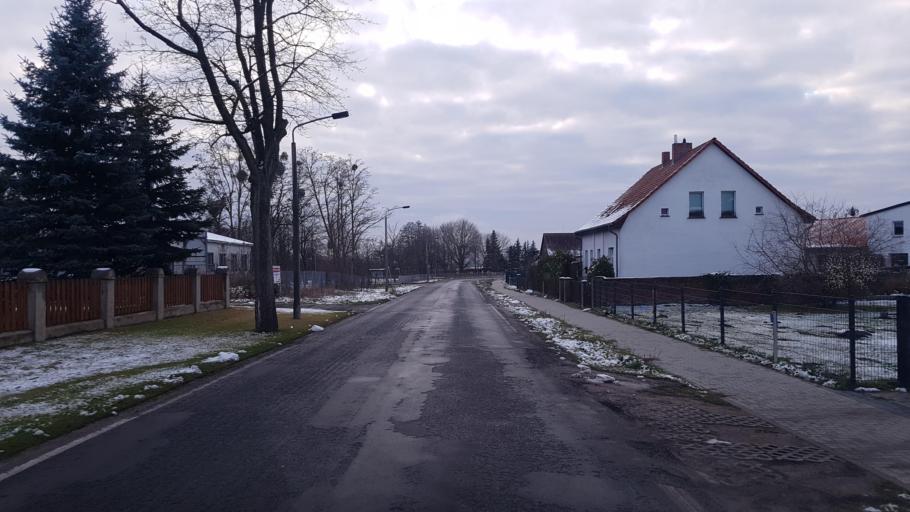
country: DE
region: Brandenburg
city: Rehfelde
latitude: 52.5262
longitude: 13.9219
